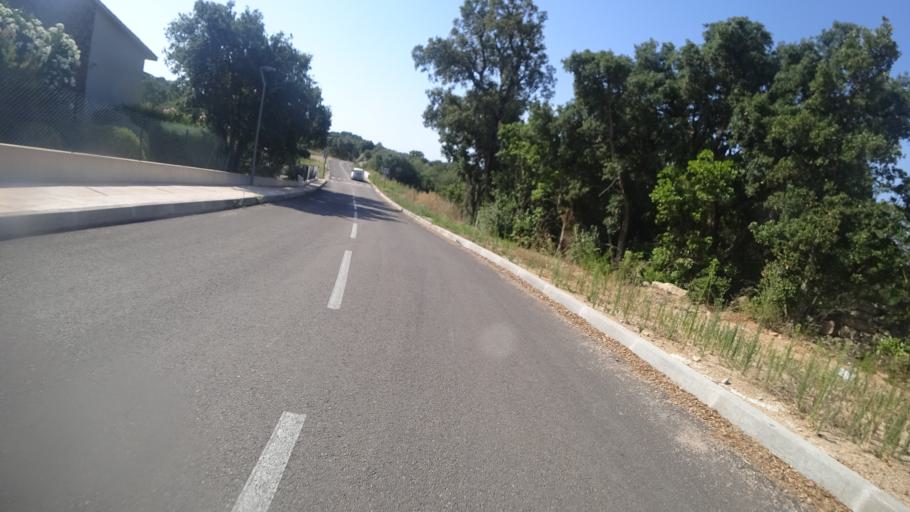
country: FR
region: Corsica
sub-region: Departement de la Corse-du-Sud
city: Porto-Vecchio
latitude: 41.6580
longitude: 9.3252
